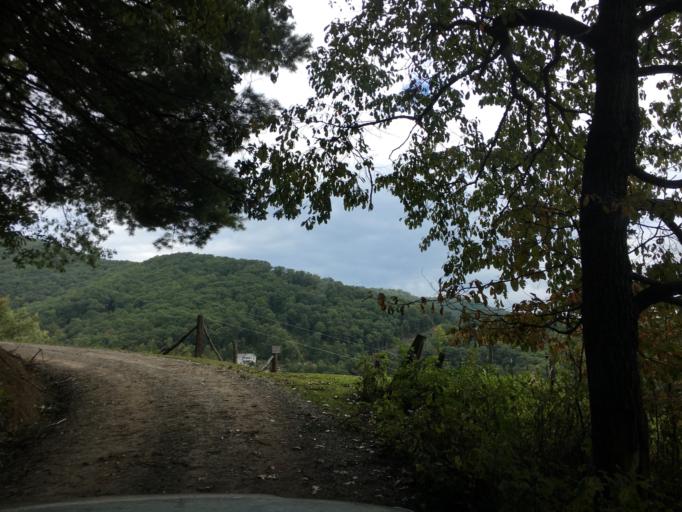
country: US
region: North Carolina
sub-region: Haywood County
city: Clyde
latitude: 35.5526
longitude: -82.9123
